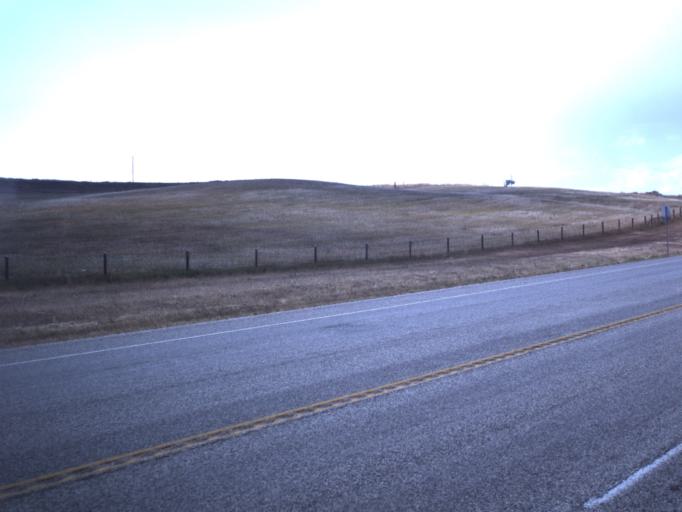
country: US
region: Utah
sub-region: Cache County
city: Mendon
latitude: 41.7640
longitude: -112.0097
